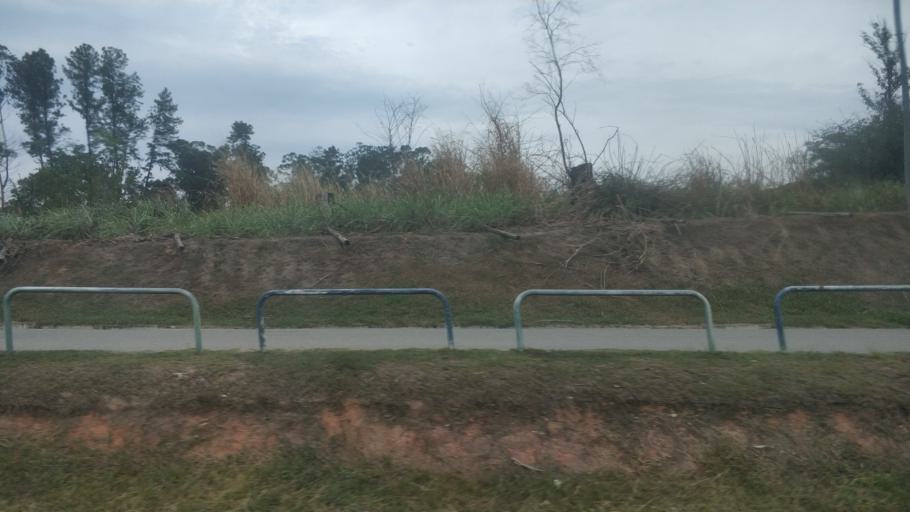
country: BR
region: Rio de Janeiro
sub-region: Seropedica
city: Seropedica
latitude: -22.7548
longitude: -43.6928
